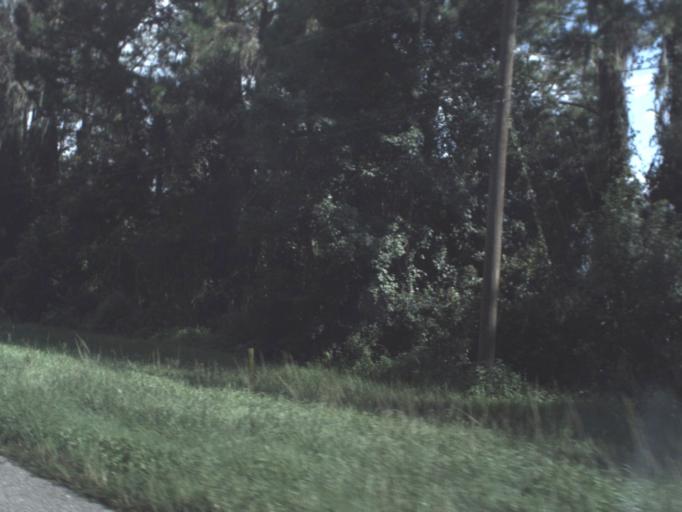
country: US
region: Florida
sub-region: Citrus County
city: Sugarmill Woods
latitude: 28.6631
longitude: -82.4670
